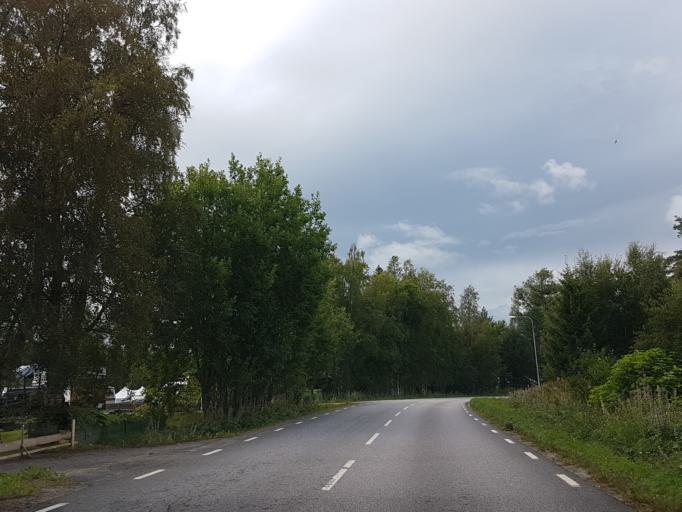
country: SE
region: Vaesterbotten
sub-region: Umea Kommun
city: Holmsund
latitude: 63.7815
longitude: 20.3858
